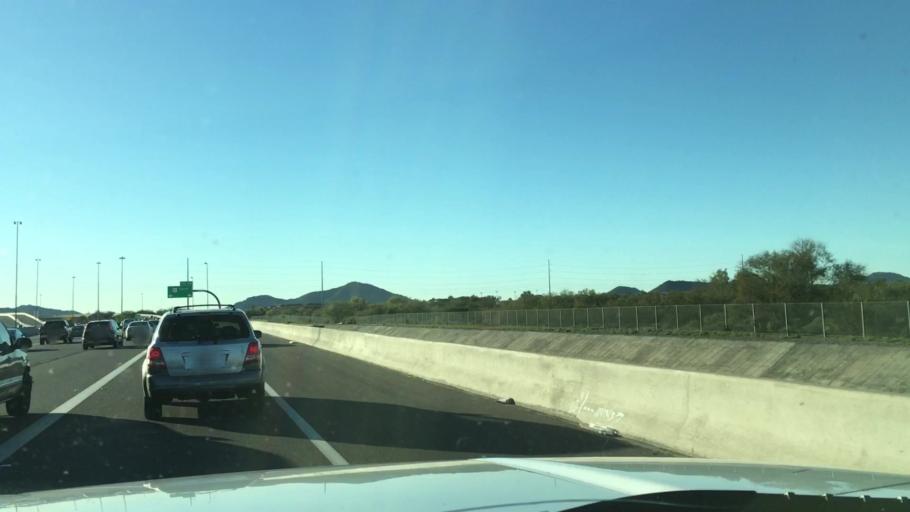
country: US
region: Arizona
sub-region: Maricopa County
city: Paradise Valley
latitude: 33.6735
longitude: -111.9892
